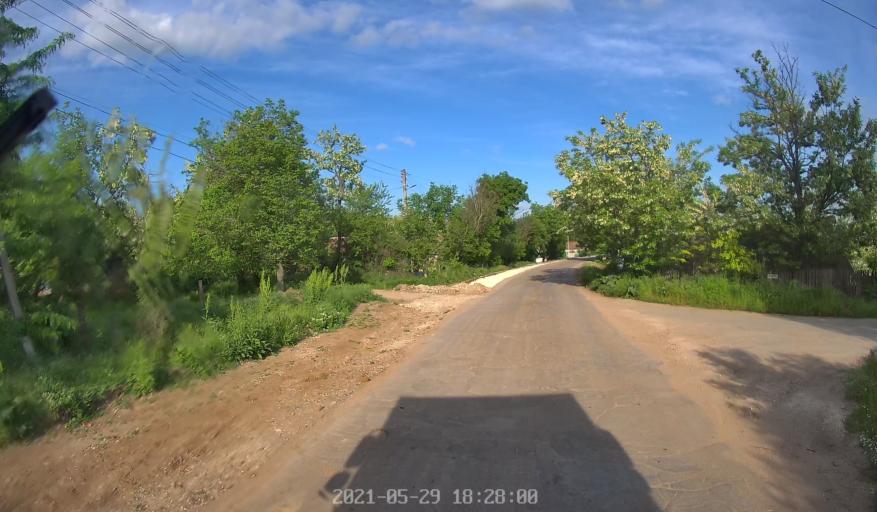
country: MD
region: Chisinau
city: Singera
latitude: 46.8295
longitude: 28.8641
